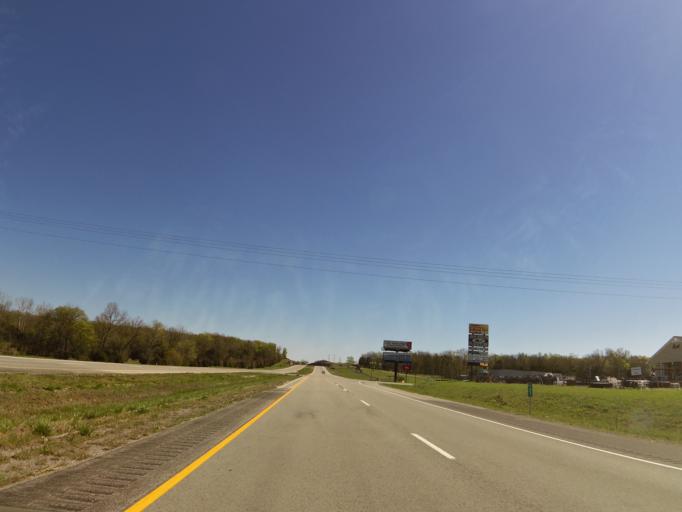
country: US
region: Kentucky
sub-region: Logan County
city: Auburn
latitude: 36.8567
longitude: -86.7509
